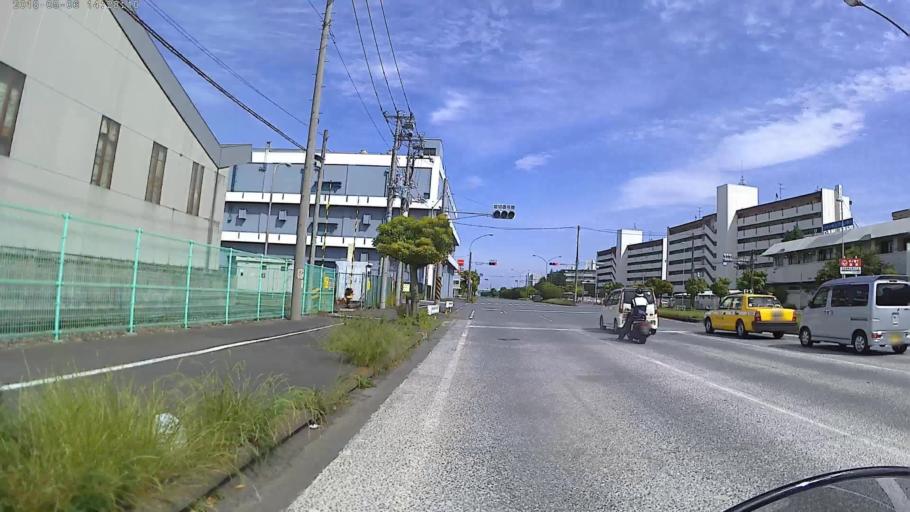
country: JP
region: Kanagawa
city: Yokohama
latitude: 35.4305
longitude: 139.6728
